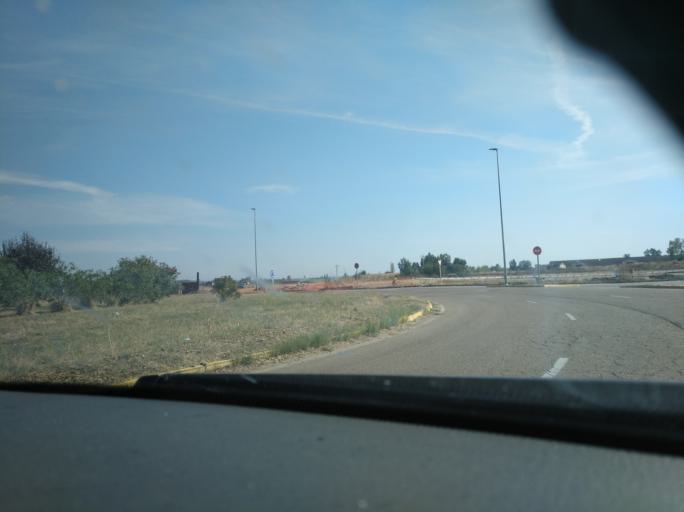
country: ES
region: Extremadura
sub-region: Provincia de Badajoz
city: Badajoz
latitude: 38.8782
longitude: -7.0263
